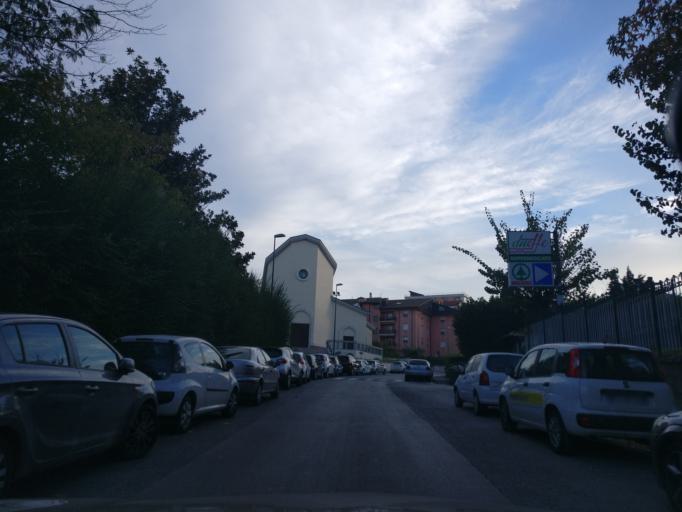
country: IT
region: Campania
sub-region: Provincia di Avellino
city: Avellino
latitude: 40.9104
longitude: 14.7922
